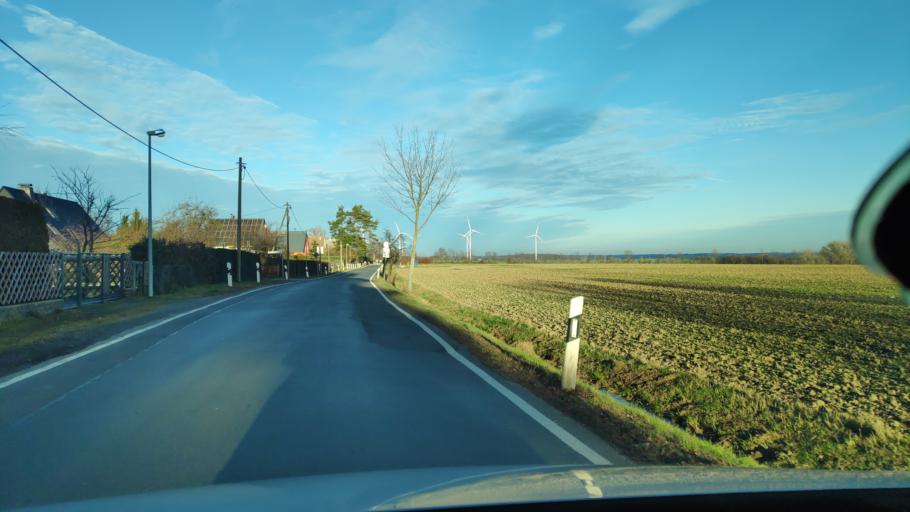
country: DE
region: Thuringia
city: Thonhausen
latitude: 50.8087
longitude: 12.3132
